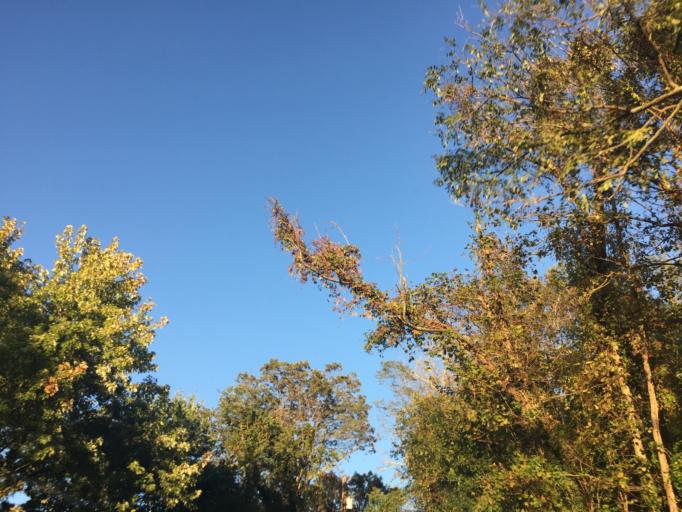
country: US
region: Maryland
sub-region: Harford County
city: Joppatowne
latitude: 39.4654
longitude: -76.3681
